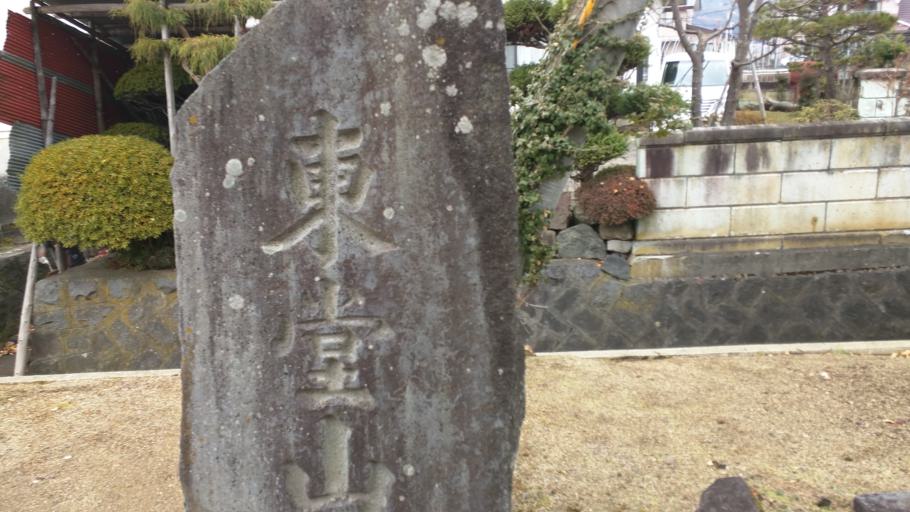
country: JP
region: Fukushima
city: Inawashiro
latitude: 37.5504
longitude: 140.0998
